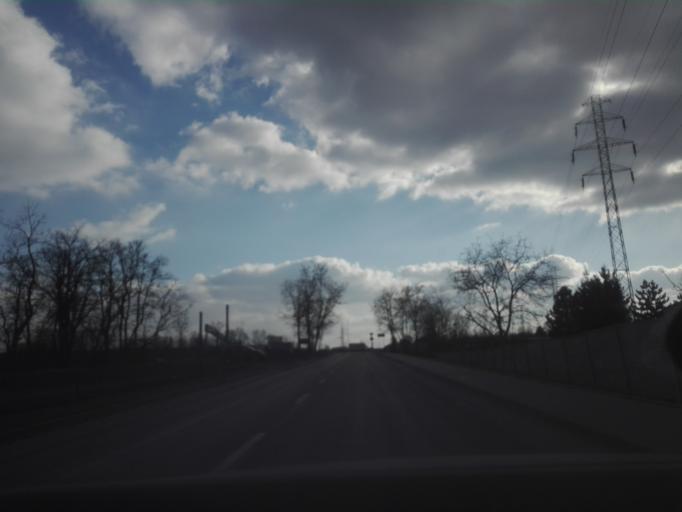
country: PL
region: Silesian Voivodeship
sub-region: Katowice
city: Katowice
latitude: 50.2533
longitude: 18.9914
